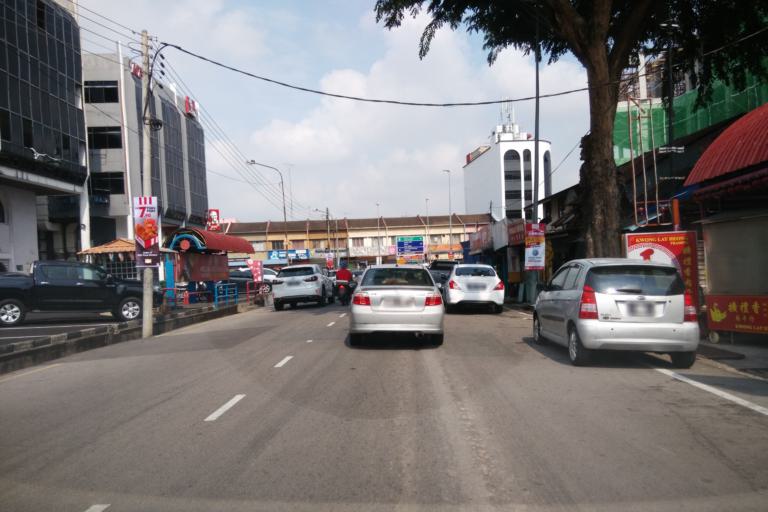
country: MY
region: Melaka
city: Malacca
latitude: 2.2078
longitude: 102.2436
